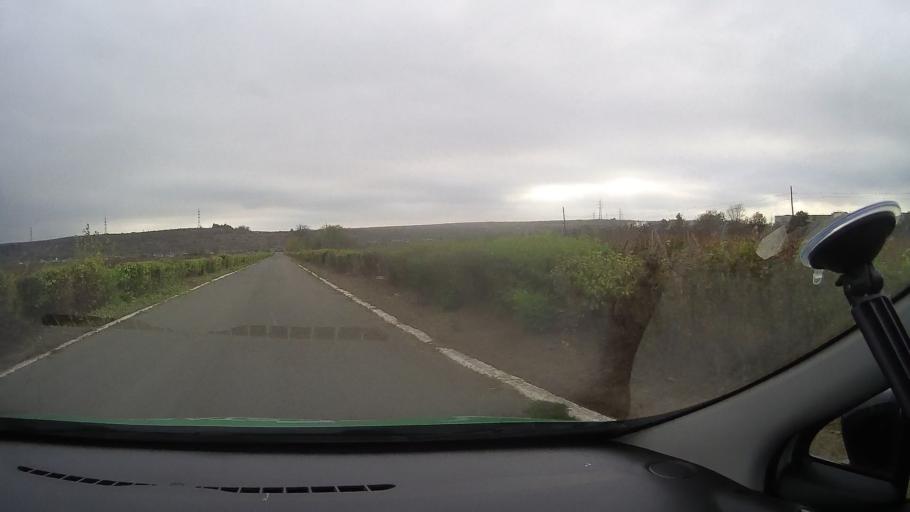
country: RO
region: Constanta
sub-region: Oras Murfatlar
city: Murfatlar
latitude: 44.1755
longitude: 28.4228
